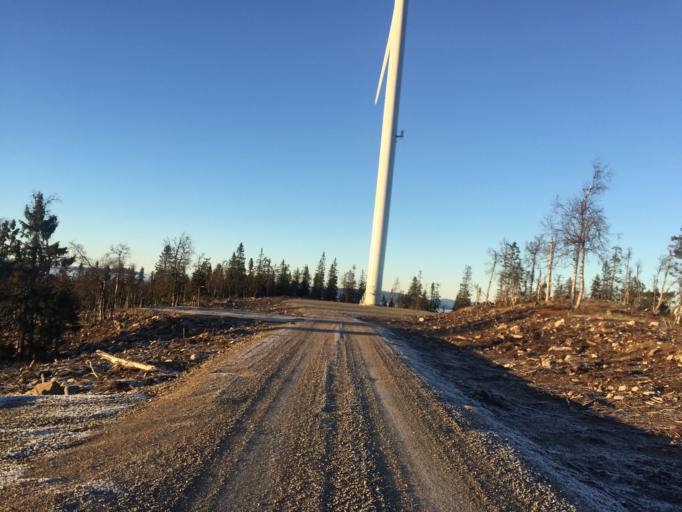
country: NO
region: Hedmark
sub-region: Elverum
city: Elverum
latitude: 61.2128
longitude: 11.7796
